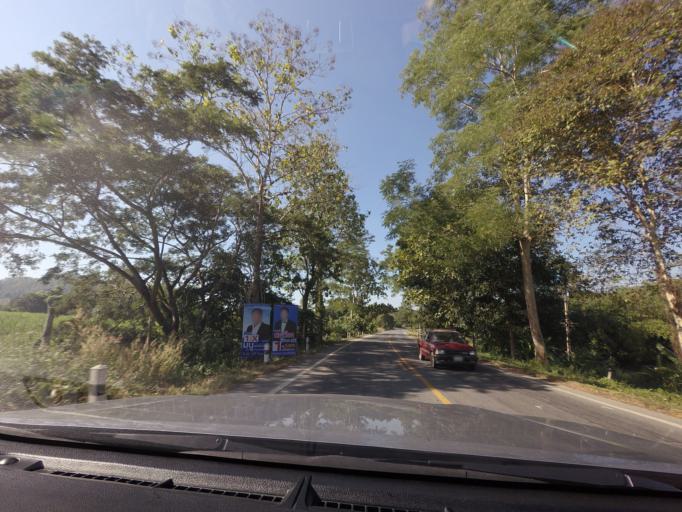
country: TH
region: Sukhothai
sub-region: Amphoe Si Satchanalai
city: Si Satchanalai
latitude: 17.6185
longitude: 99.7070
